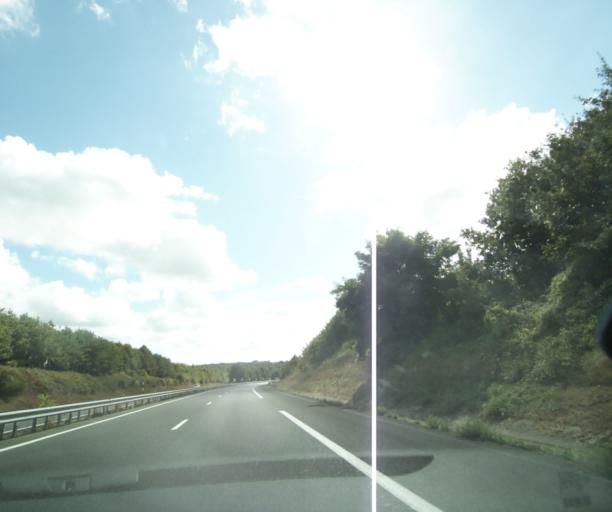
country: FR
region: Poitou-Charentes
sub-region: Departement de la Charente-Maritime
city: Bussac-sur-Charente
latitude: 45.7976
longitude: -0.6717
